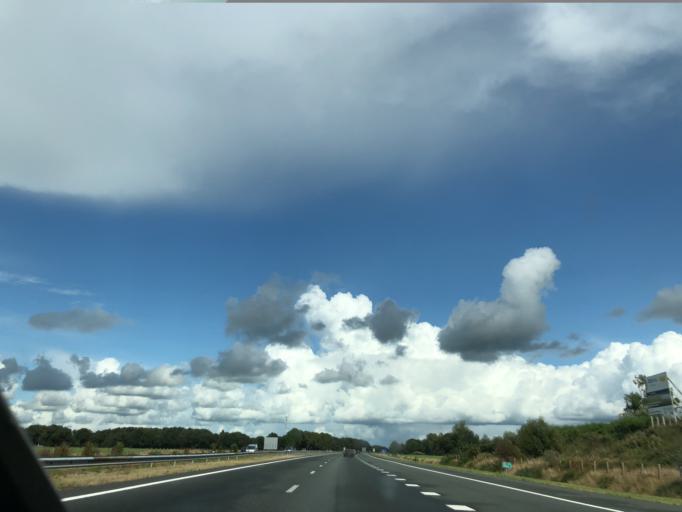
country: NL
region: Friesland
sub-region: Gemeente Smallingerland
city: Drachtstercompagnie
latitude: 53.1315
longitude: 6.1911
